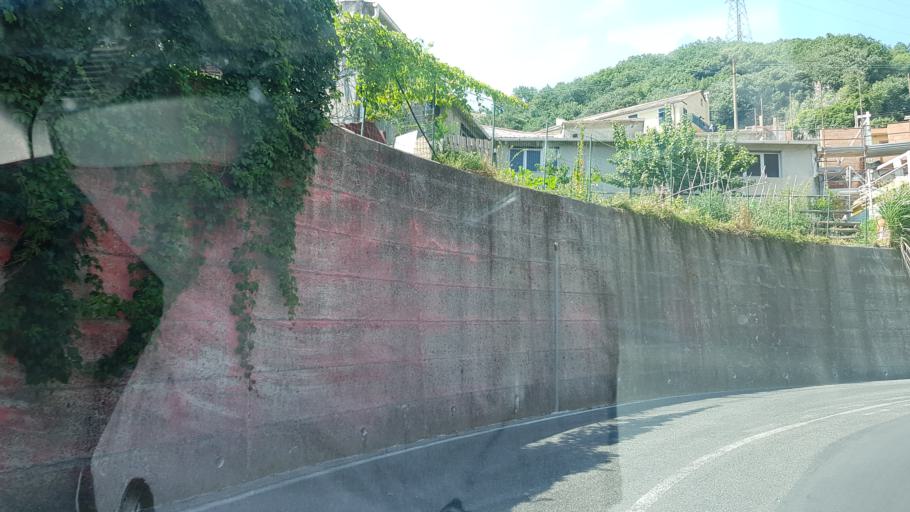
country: IT
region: Liguria
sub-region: Provincia di Genova
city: San Teodoro
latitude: 44.4352
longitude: 8.8681
